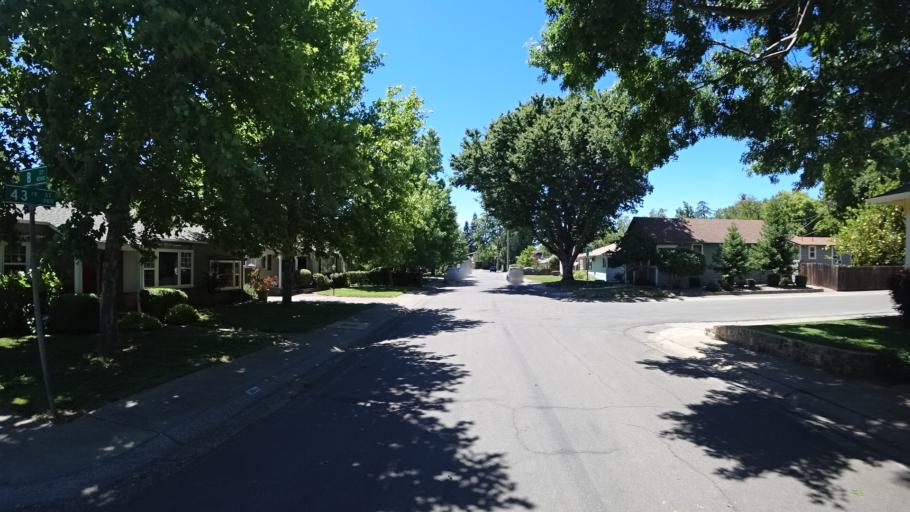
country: US
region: California
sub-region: Sacramento County
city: Sacramento
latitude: 38.5767
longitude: -121.4457
